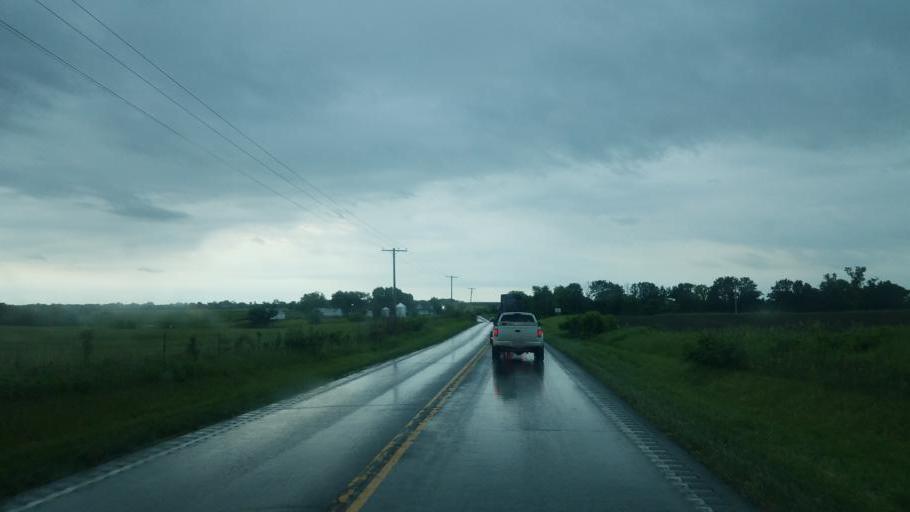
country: US
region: Missouri
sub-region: Cooper County
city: Boonville
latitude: 38.8822
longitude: -92.6510
